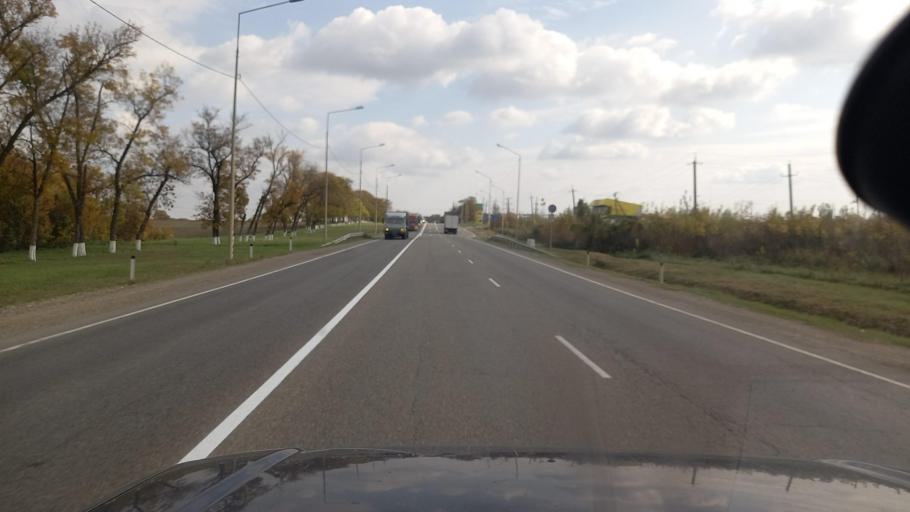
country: RU
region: Krasnodarskiy
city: Kholmskiy
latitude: 44.8480
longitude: 38.4159
